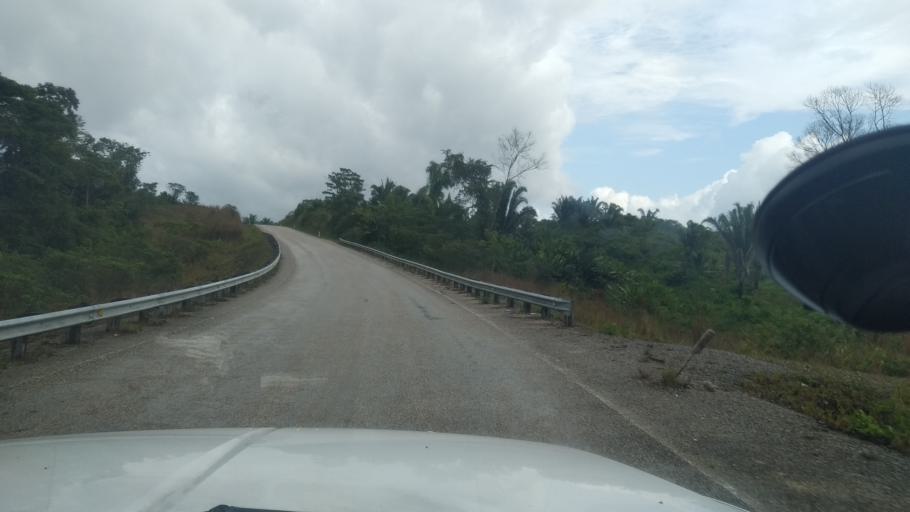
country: GT
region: Peten
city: San Luis
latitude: 16.1958
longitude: -89.1632
